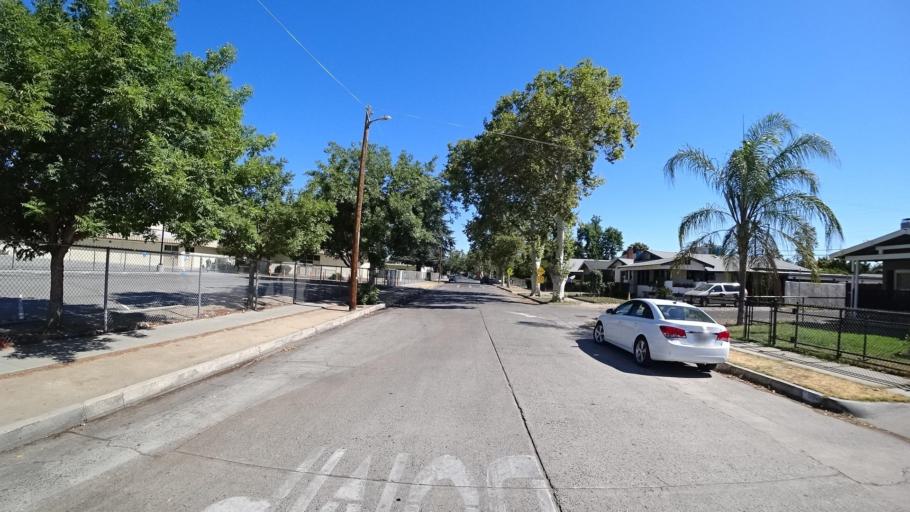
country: US
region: California
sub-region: Fresno County
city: Fresno
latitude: 36.7548
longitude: -119.8064
